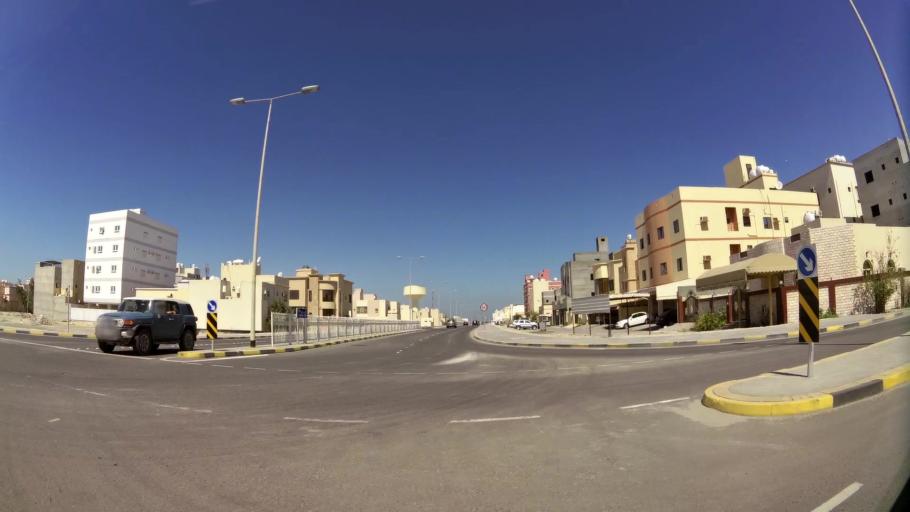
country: BH
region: Muharraq
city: Al Hadd
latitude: 26.2765
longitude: 50.6411
